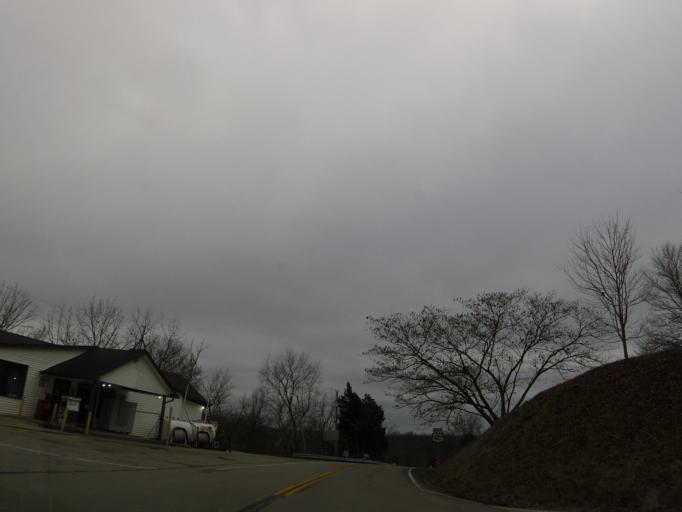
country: US
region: Kentucky
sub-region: Franklin County
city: Frankfort
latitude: 38.2733
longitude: -84.9442
